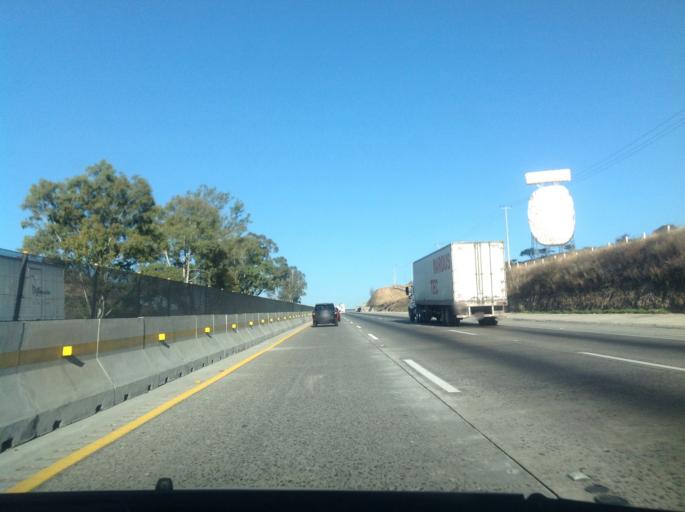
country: MX
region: Hidalgo
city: Tepeji de Ocampo
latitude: 19.9152
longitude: -99.3635
